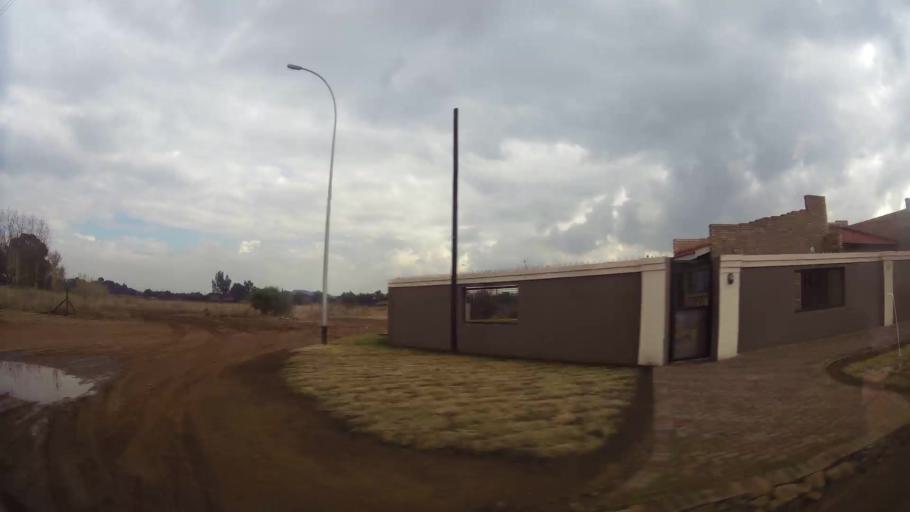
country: ZA
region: Gauteng
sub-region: Sedibeng District Municipality
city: Meyerton
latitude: -26.5805
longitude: 28.0027
